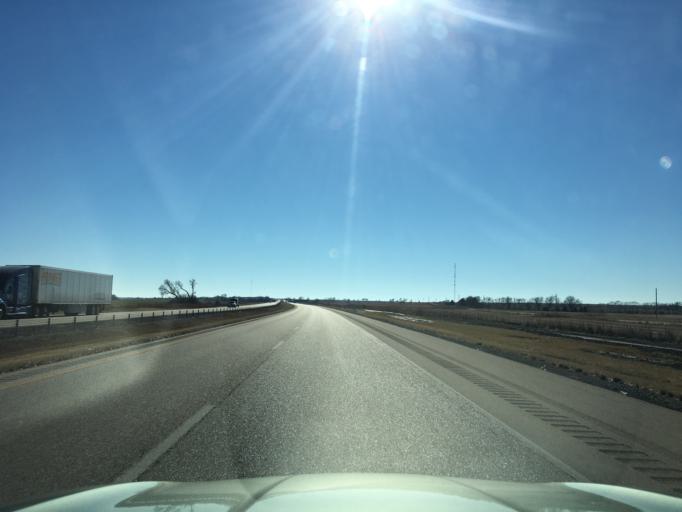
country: US
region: Oklahoma
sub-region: Kay County
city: Blackwell
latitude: 36.8953
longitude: -97.3541
